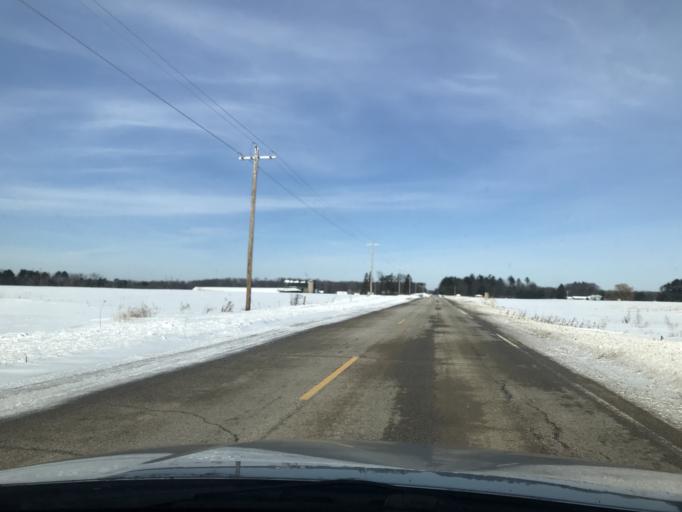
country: US
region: Wisconsin
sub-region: Oconto County
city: Oconto Falls
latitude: 45.1290
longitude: -88.1777
